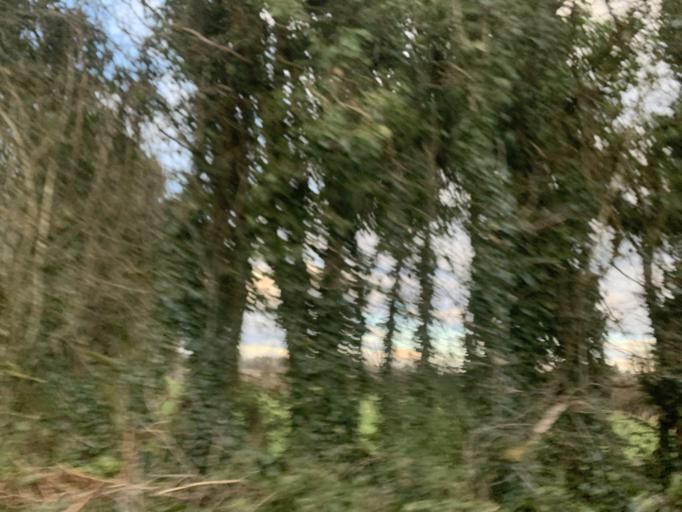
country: IE
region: Connaught
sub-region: Maigh Eo
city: Ballyhaunis
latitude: 53.8430
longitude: -8.7232
